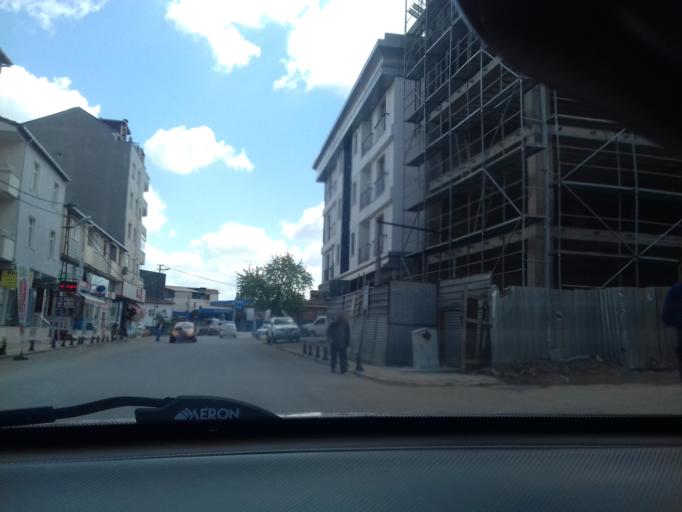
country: TR
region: Istanbul
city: Pendik
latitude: 40.8866
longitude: 29.2851
